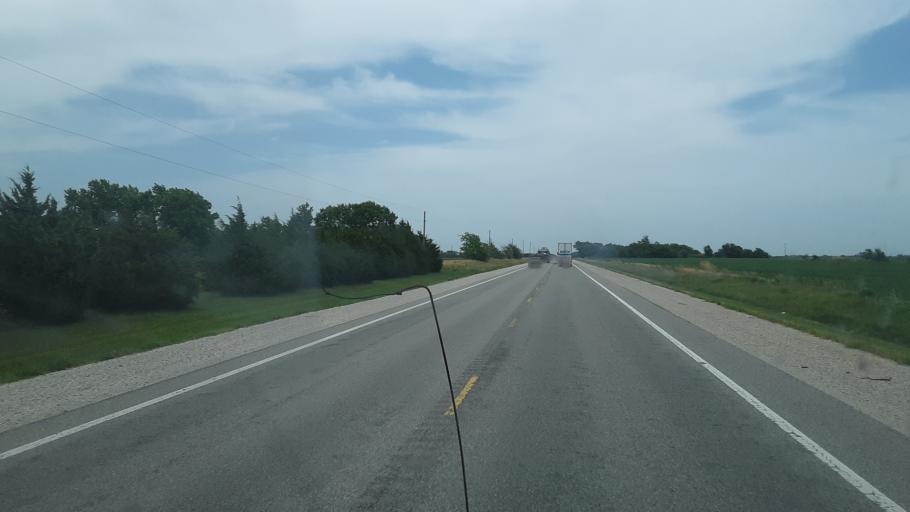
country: US
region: Kansas
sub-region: Allen County
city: Iola
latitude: 37.9216
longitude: -95.2126
